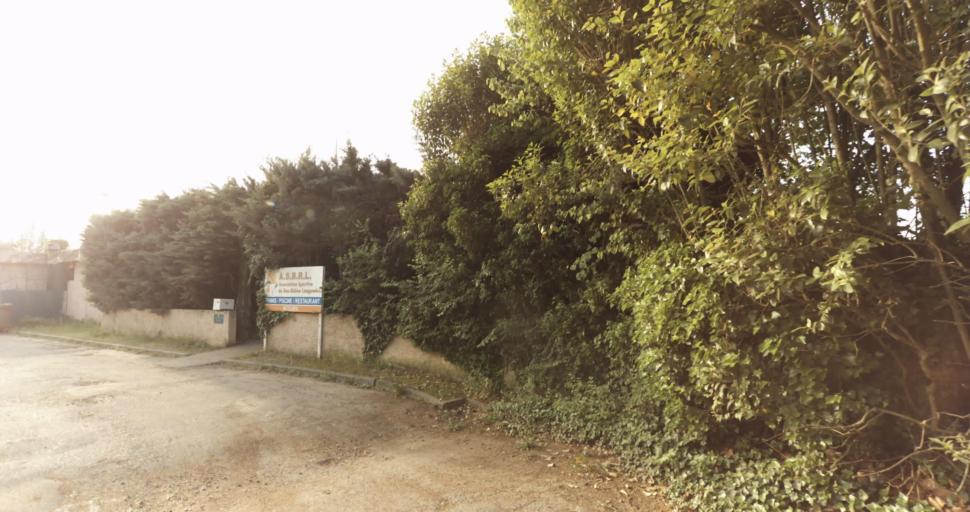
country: FR
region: Languedoc-Roussillon
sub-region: Departement du Gard
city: Caissargues
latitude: 43.8198
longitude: 4.3882
